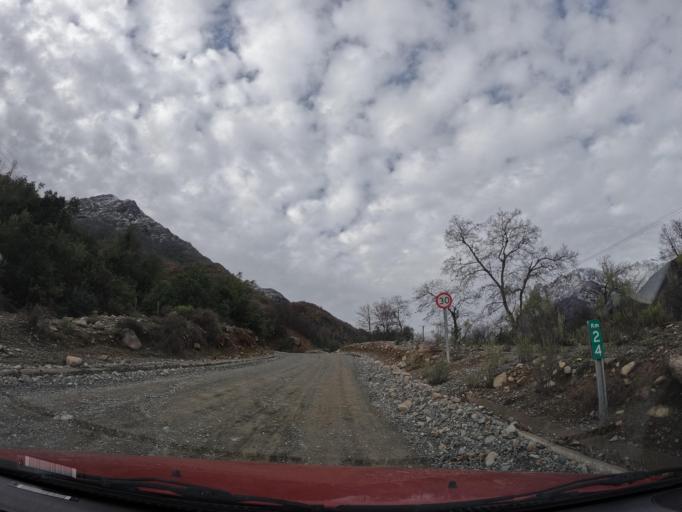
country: CL
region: Maule
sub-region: Provincia de Linares
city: Colbun
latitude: -35.8584
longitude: -71.2330
